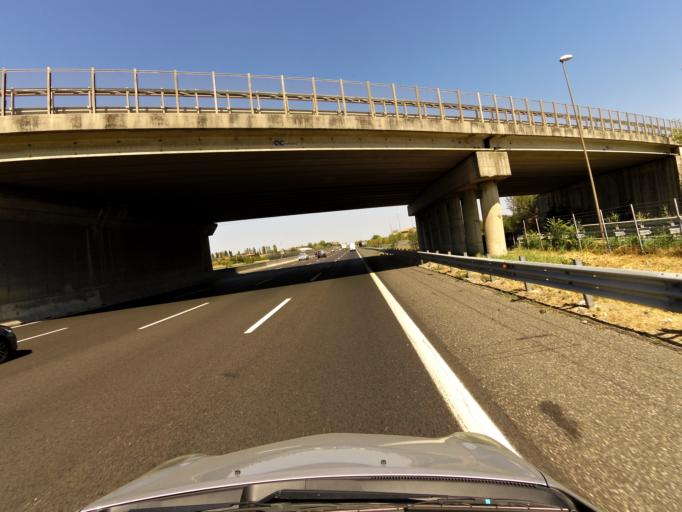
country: IT
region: Emilia-Romagna
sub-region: Provincia di Modena
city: Baggiovara
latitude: 44.6284
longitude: 10.8788
